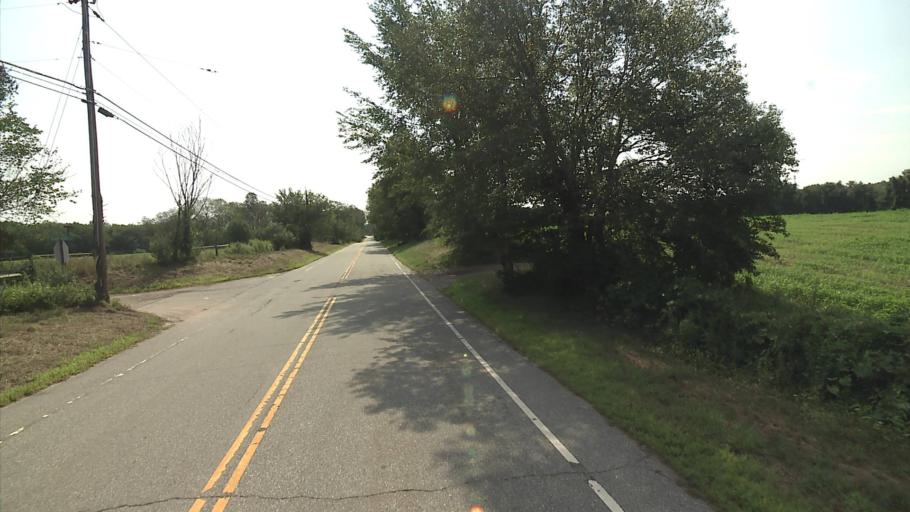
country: US
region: Connecticut
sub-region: New London County
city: Colchester
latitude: 41.5739
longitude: -72.2576
